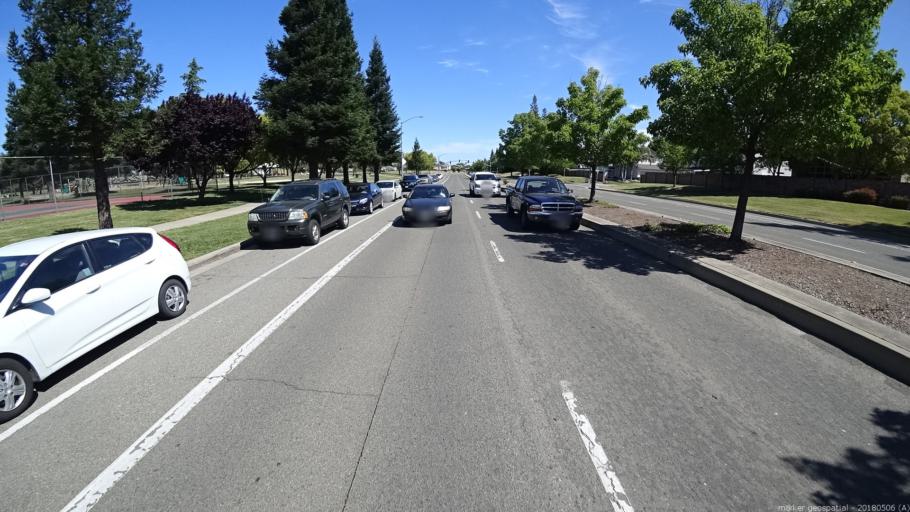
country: US
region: California
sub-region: Sacramento County
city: Laguna
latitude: 38.4434
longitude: -121.4260
